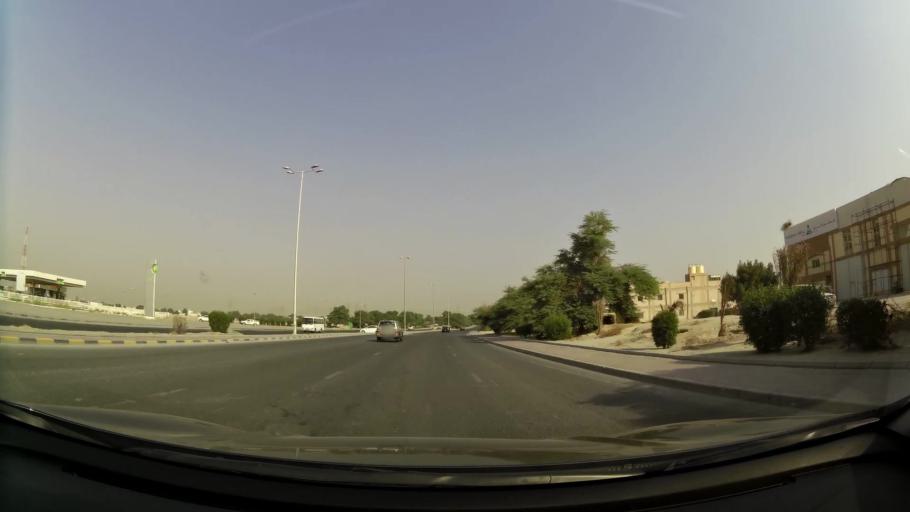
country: KW
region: Al Asimah
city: Ar Rabiyah
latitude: 29.2868
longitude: 47.8322
